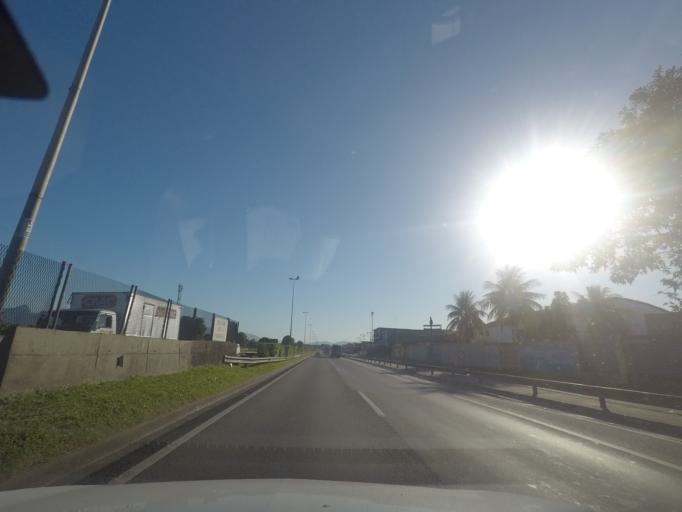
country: BR
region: Rio de Janeiro
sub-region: Duque De Caxias
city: Duque de Caxias
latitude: -22.6693
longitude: -43.2712
